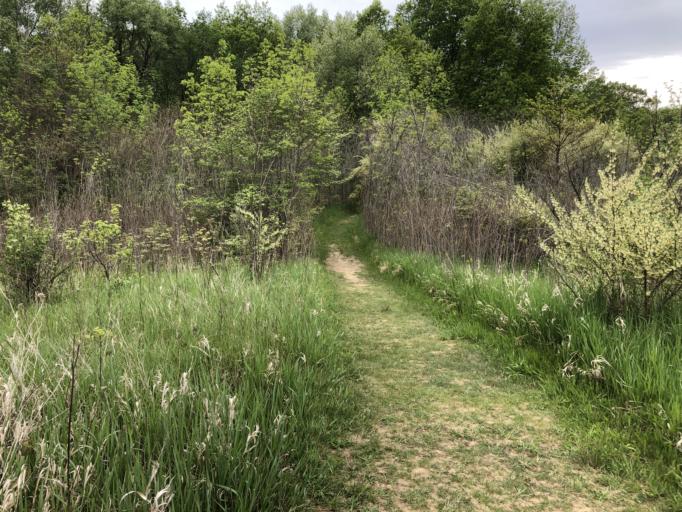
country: US
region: Indiana
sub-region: Steuben County
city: Angola
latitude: 41.7169
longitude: -85.0226
